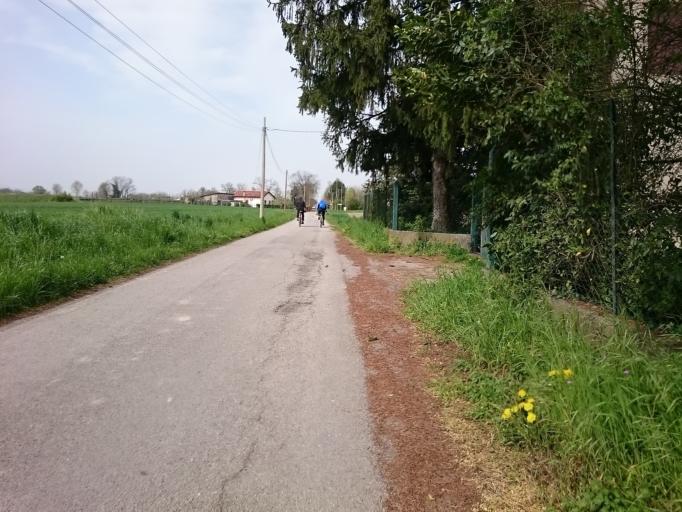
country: IT
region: Veneto
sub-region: Provincia di Padova
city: Tribano
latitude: 45.1829
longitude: 11.8423
